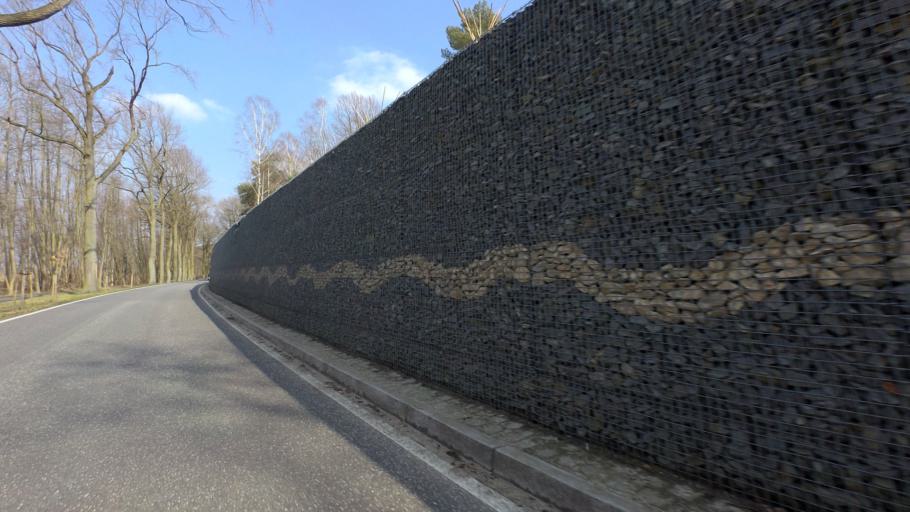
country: DE
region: Brandenburg
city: Werder
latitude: 52.3151
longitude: 12.9449
